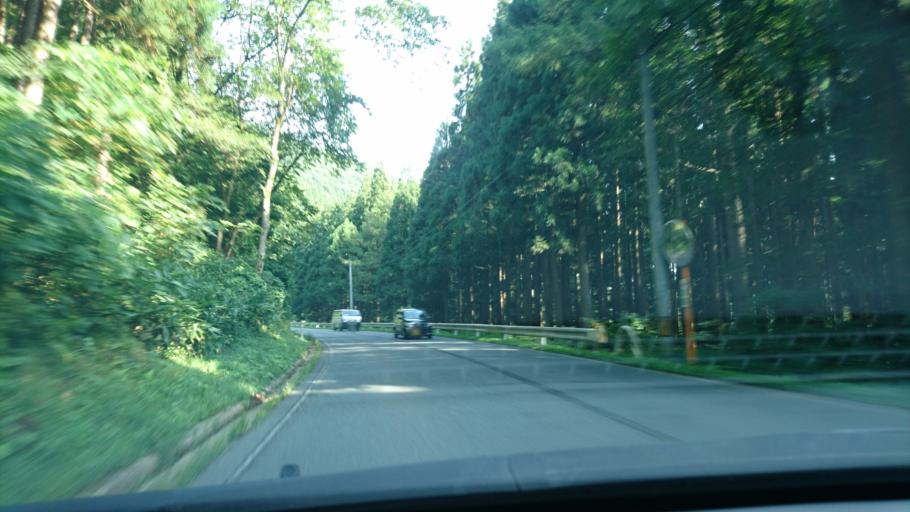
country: JP
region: Akita
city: Yokotemachi
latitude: 39.3111
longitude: 140.8065
